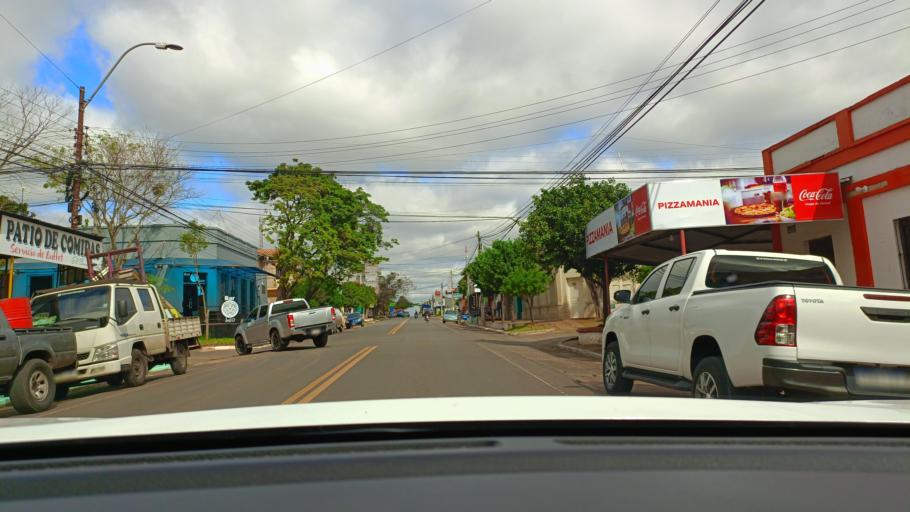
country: PY
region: San Pedro
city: Guayaybi
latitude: -24.6684
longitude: -56.4450
